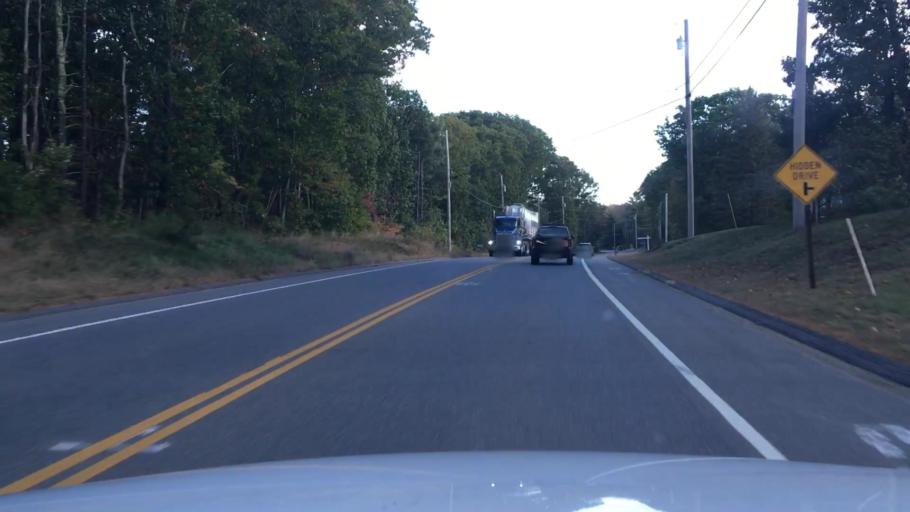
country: US
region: Maine
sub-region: York County
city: Wells Beach Station
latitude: 43.3400
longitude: -70.6370
